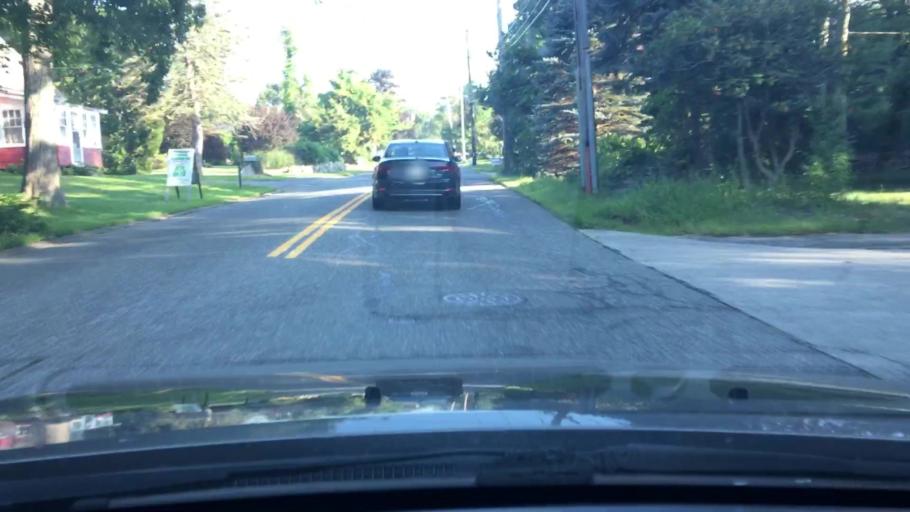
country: US
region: Massachusetts
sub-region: Worcester County
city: Milford
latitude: 42.1795
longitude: -71.5365
